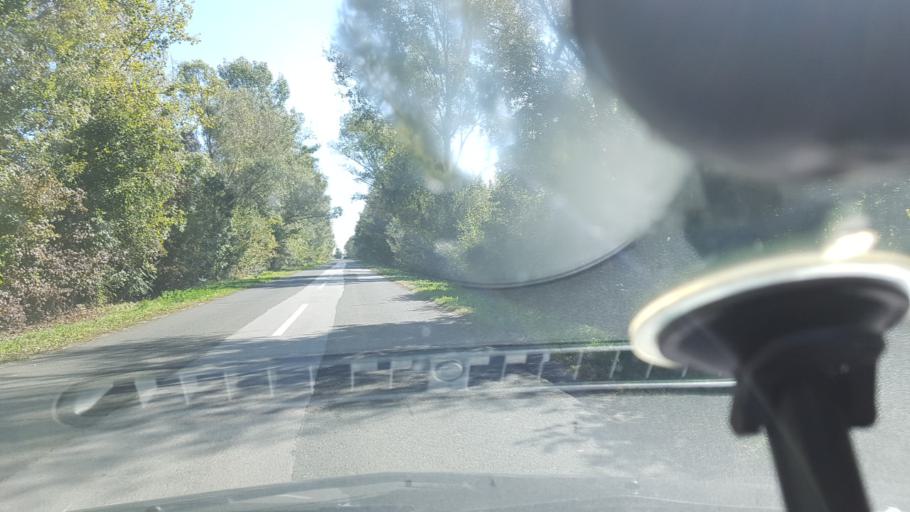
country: HR
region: Zagrebacka
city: Brckovljani
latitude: 45.7594
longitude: 16.2706
